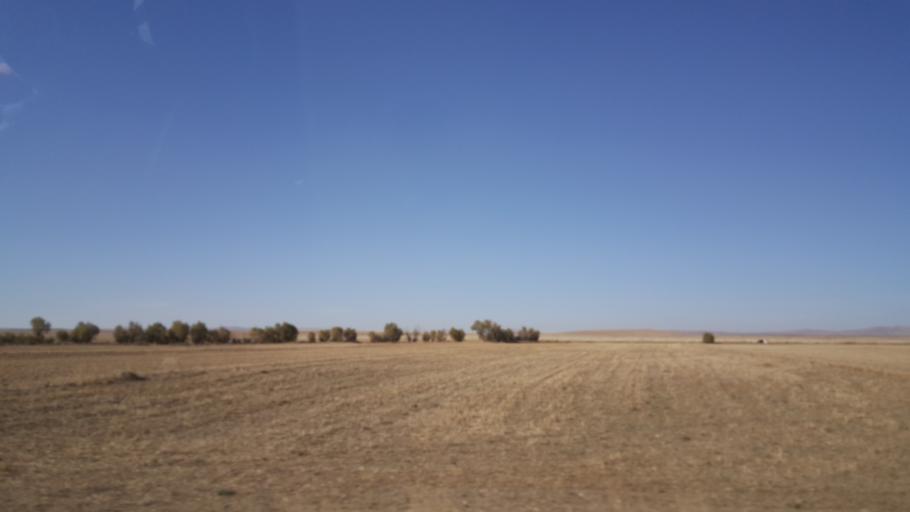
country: TR
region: Ankara
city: Yenice
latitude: 39.3778
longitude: 32.8167
